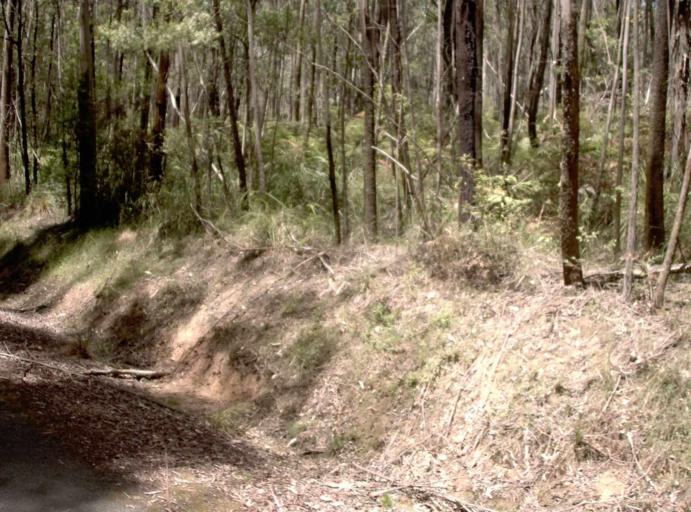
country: AU
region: New South Wales
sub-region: Bombala
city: Bombala
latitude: -37.4361
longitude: 148.9856
